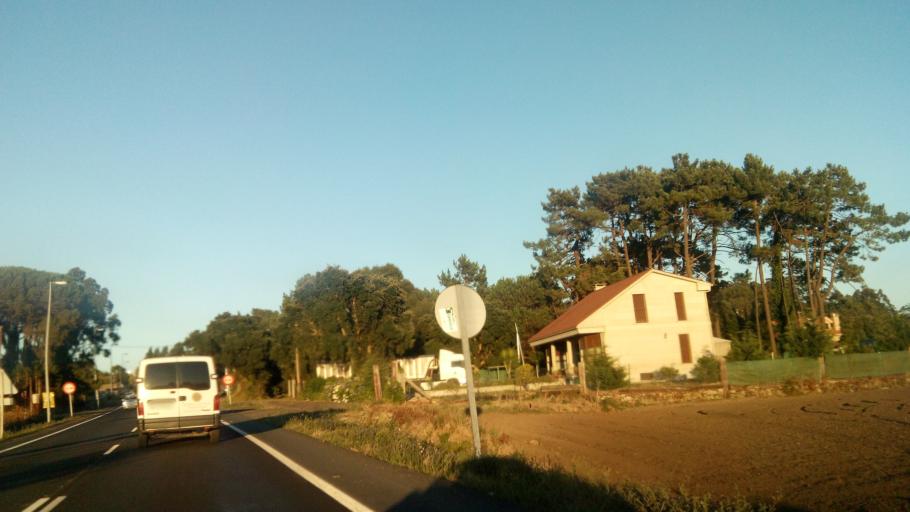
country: ES
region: Galicia
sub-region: Provincia de Pontevedra
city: Vilanova de Arousa
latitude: 42.5492
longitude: -8.8264
